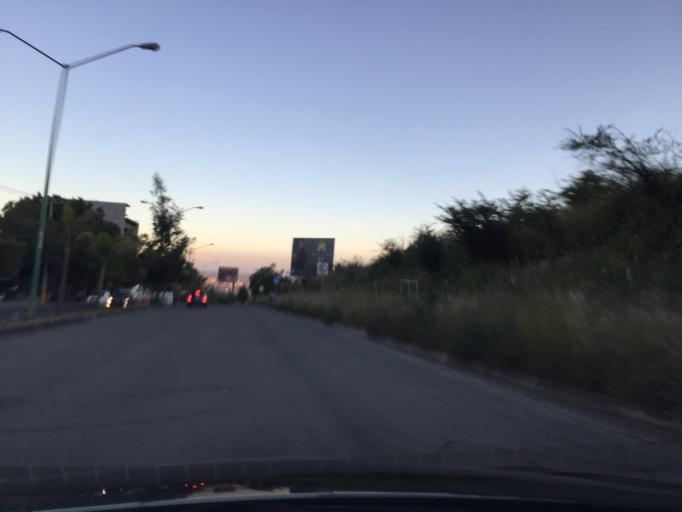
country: MX
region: Guanajuato
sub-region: Leon
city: La Ermita
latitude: 21.1632
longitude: -101.7096
